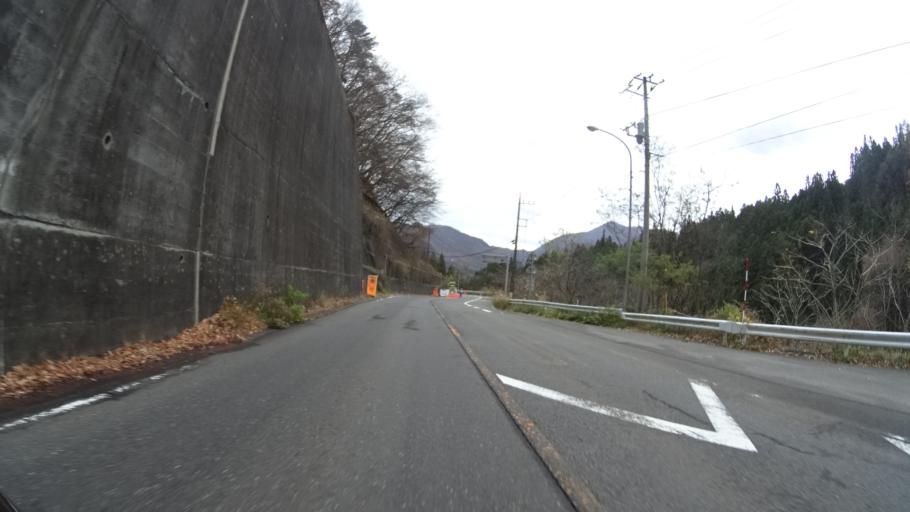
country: JP
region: Gunma
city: Nakanojomachi
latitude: 36.7340
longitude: 138.8518
